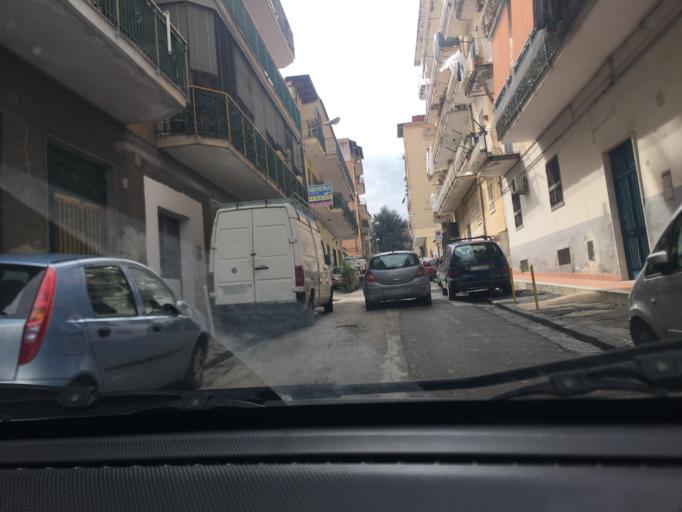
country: IT
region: Campania
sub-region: Provincia di Napoli
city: Calvizzano
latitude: 40.8967
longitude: 14.1866
